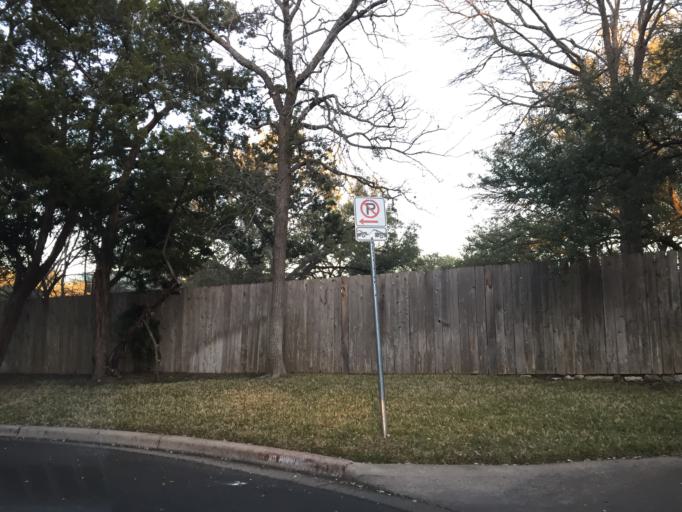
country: US
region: Texas
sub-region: Williamson County
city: Jollyville
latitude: 30.4247
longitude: -97.7596
